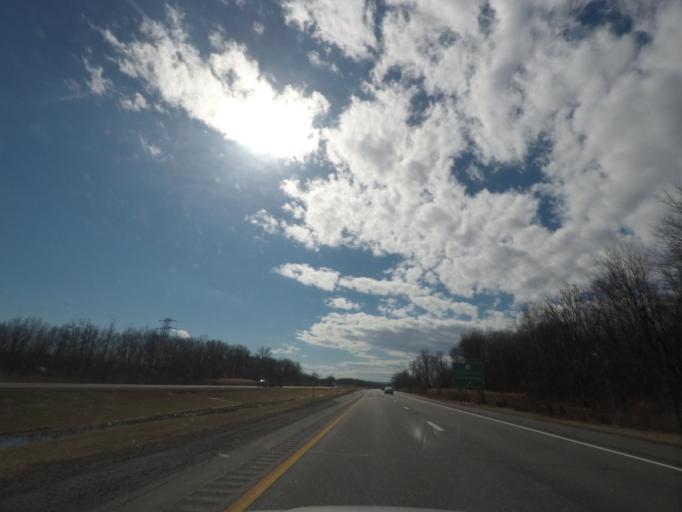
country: US
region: New York
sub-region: Madison County
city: Canastota
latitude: 43.0965
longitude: -75.7388
